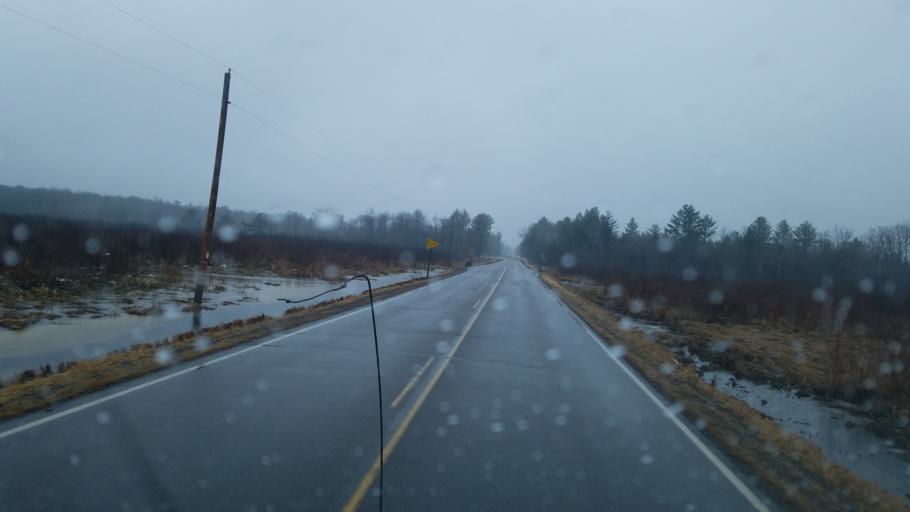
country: US
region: Wisconsin
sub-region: Wood County
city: Marshfield
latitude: 44.5091
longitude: -90.2787
